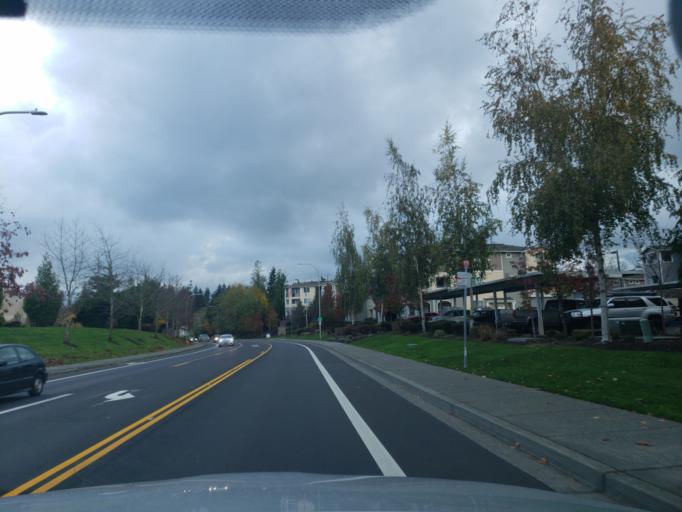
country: US
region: Washington
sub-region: Snohomish County
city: Mukilteo
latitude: 47.9437
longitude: -122.2516
